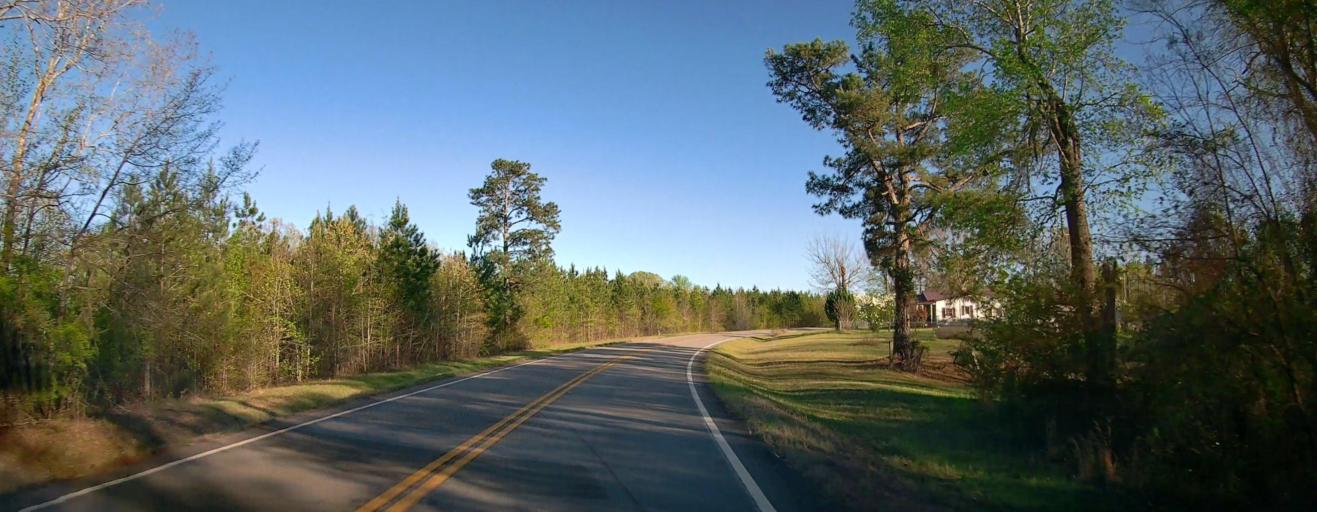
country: US
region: Georgia
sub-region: Wilkinson County
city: Irwinton
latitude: 32.9092
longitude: -83.1225
